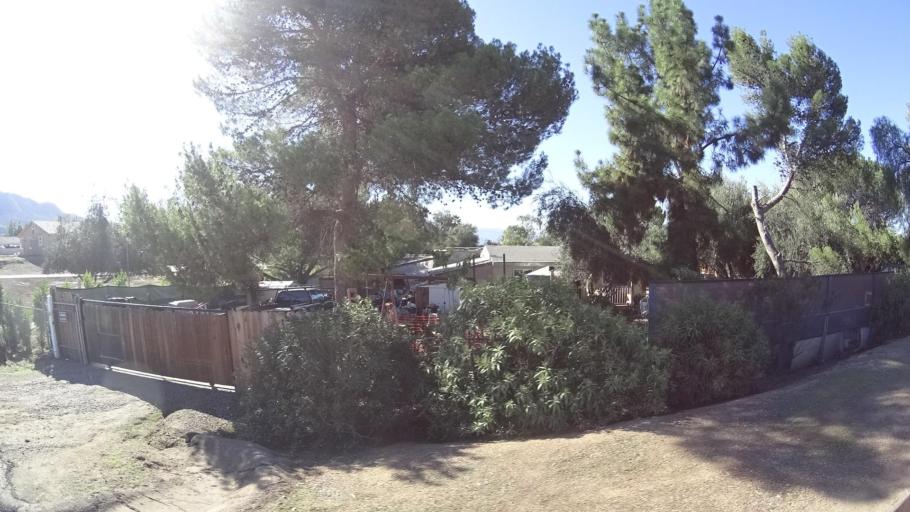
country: US
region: California
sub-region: San Diego County
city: Jamul
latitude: 32.7226
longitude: -116.8575
